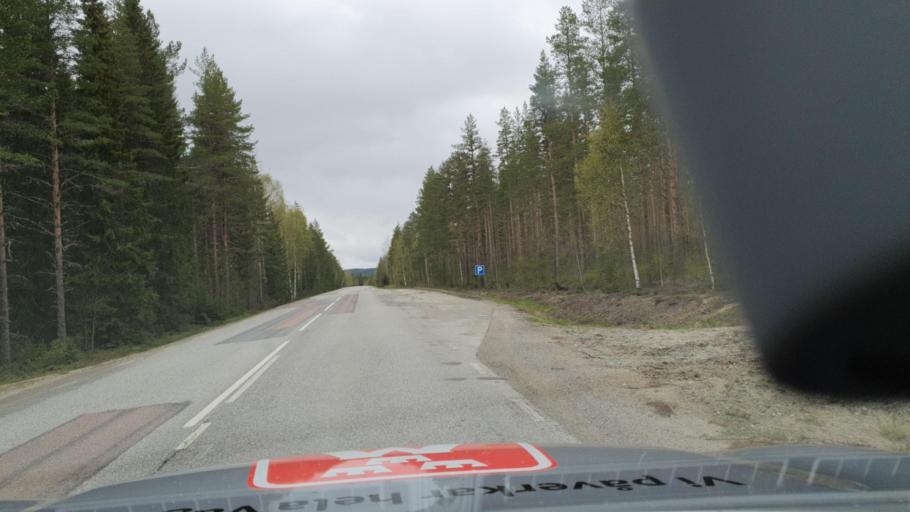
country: SE
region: Vaesternorrland
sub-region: OErnskoeldsviks Kommun
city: Bredbyn
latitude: 63.5484
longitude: 17.6938
